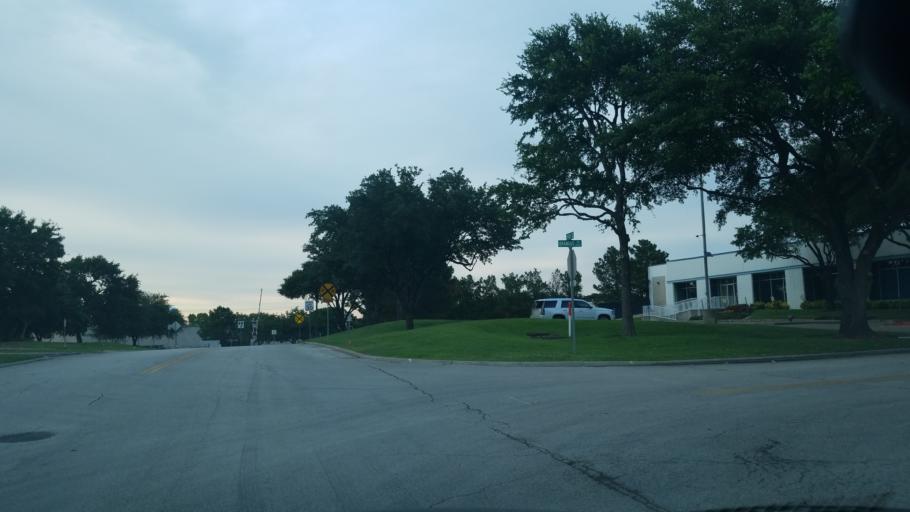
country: US
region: Texas
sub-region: Dallas County
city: Irving
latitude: 32.8744
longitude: -96.9749
